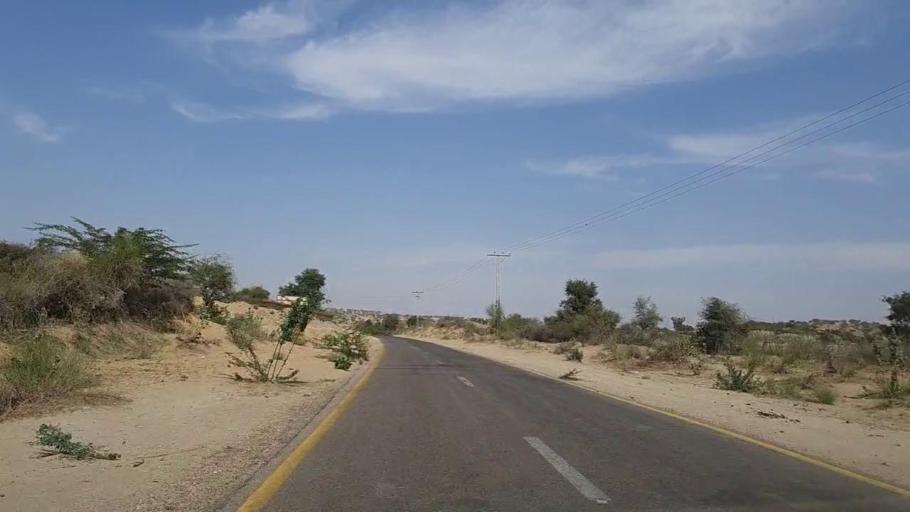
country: PK
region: Sindh
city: Mithi
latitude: 24.7948
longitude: 69.8149
